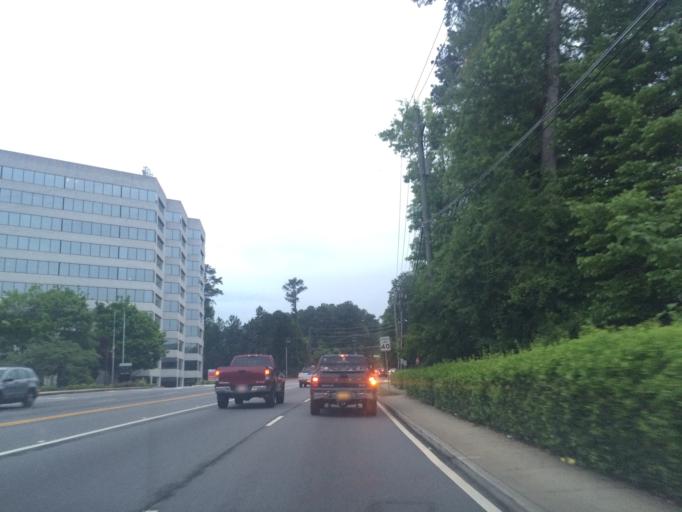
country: US
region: Georgia
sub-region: DeKalb County
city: North Druid Hills
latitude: 33.8435
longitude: -84.3146
